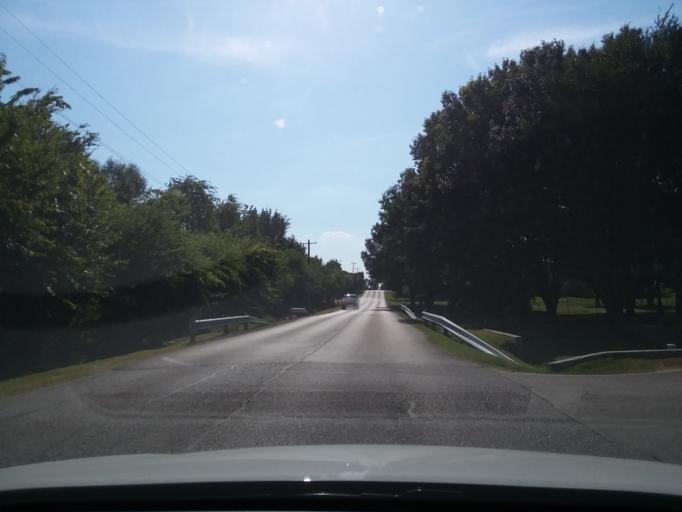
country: US
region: Texas
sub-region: Denton County
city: Double Oak
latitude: 33.0584
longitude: -97.1027
